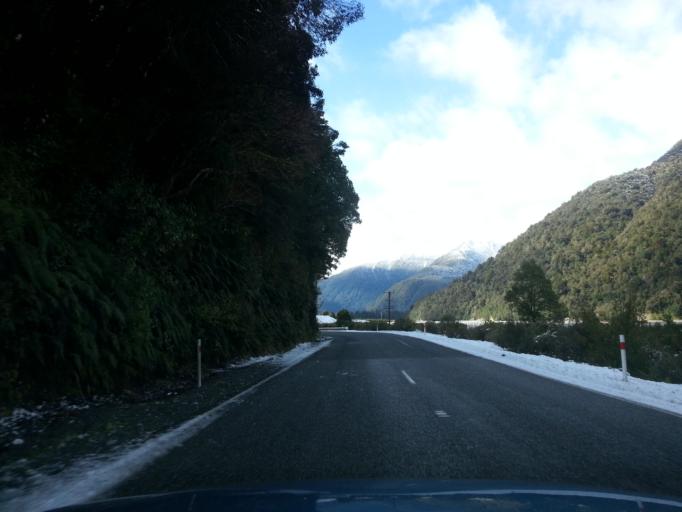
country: NZ
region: West Coast
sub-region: Grey District
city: Greymouth
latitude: -42.8069
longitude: 171.5700
